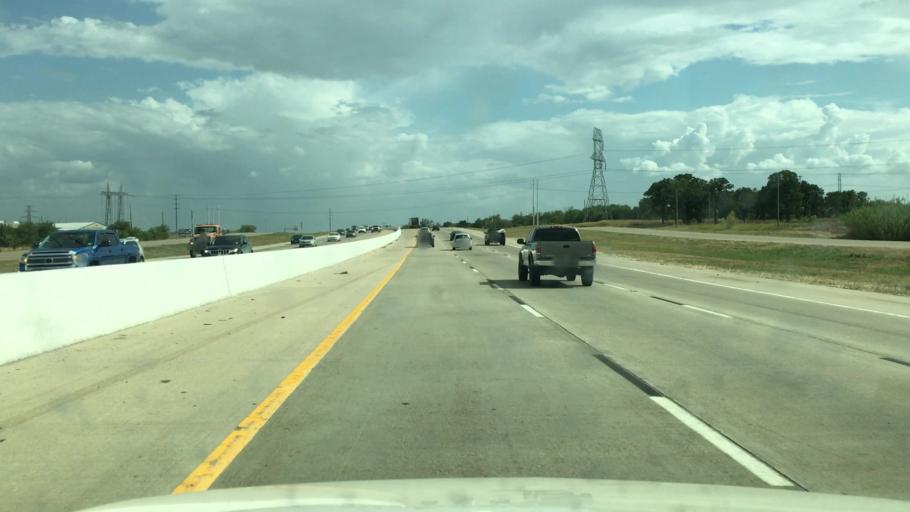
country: US
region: Texas
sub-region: McLennan County
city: Northcrest
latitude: 31.7044
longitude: -97.1024
